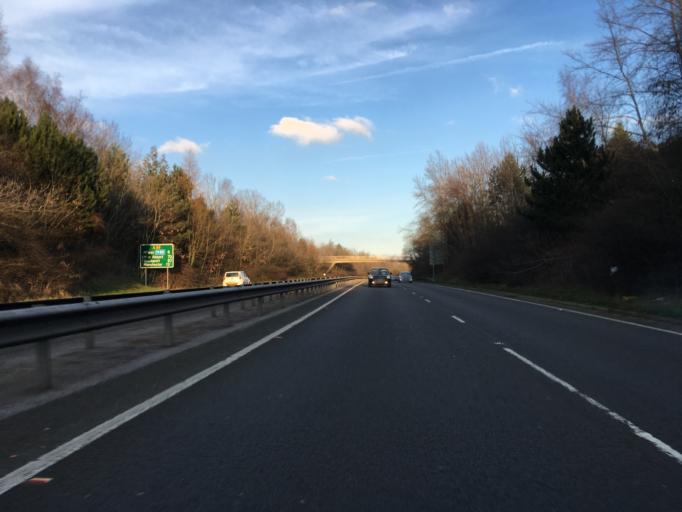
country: GB
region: England
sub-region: Cheshire East
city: Wilmslow
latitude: 53.3359
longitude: -2.2111
